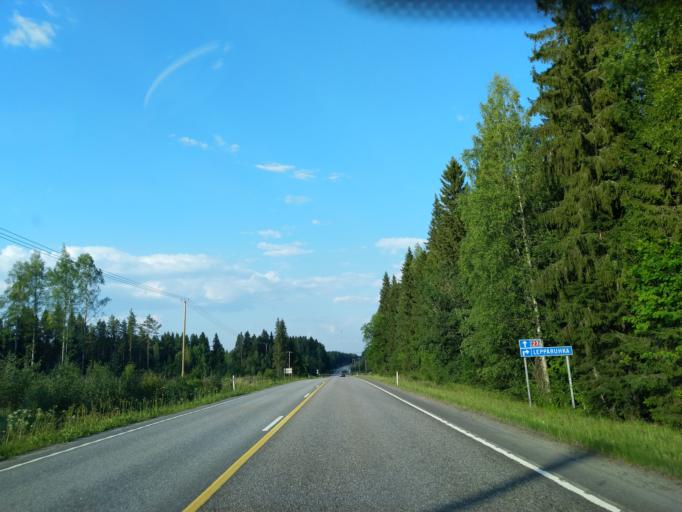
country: FI
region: Satakunta
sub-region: Pori
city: Laengelmaeki
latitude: 61.7800
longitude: 22.2020
